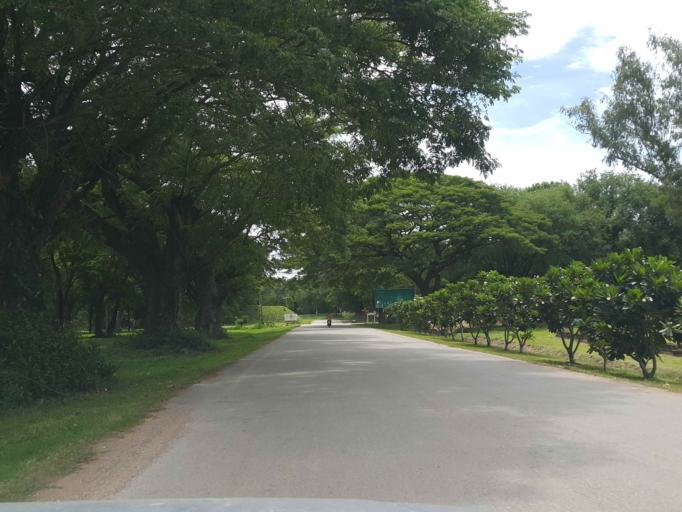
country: TH
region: Sukhothai
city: Ban Na
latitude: 17.0135
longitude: 99.7057
